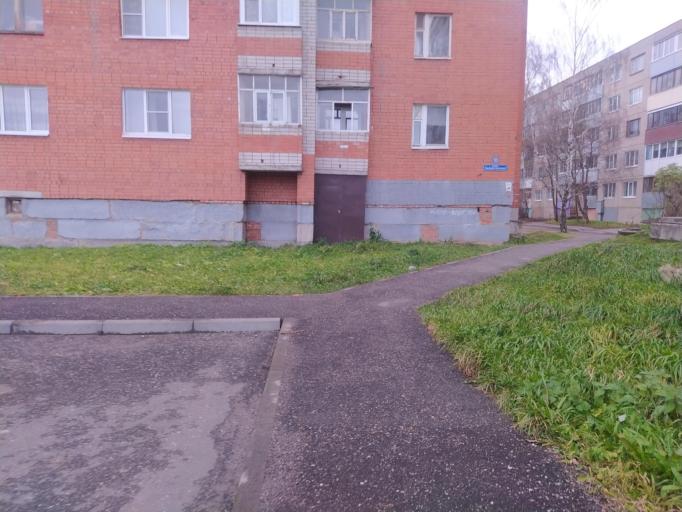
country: RU
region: Jaroslavl
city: Rybinsk
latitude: 58.0457
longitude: 38.7845
